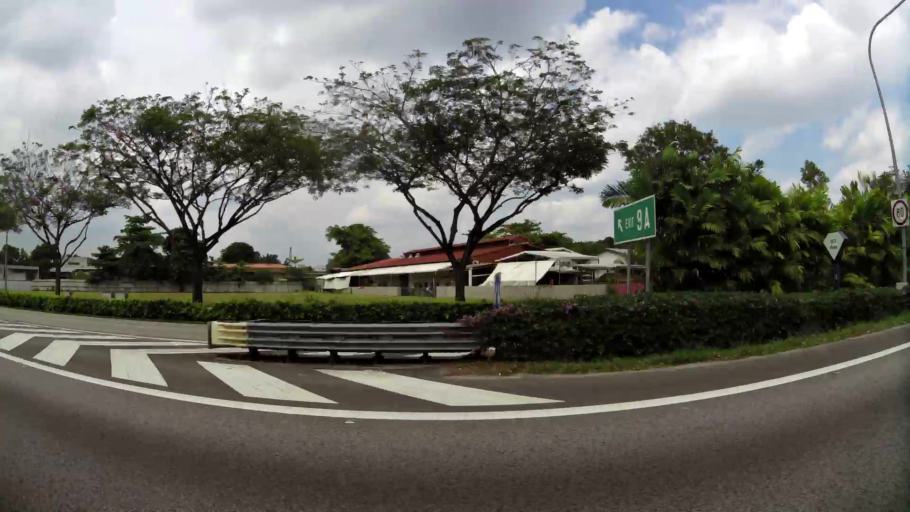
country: SG
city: Singapore
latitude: 1.3607
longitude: 103.9038
